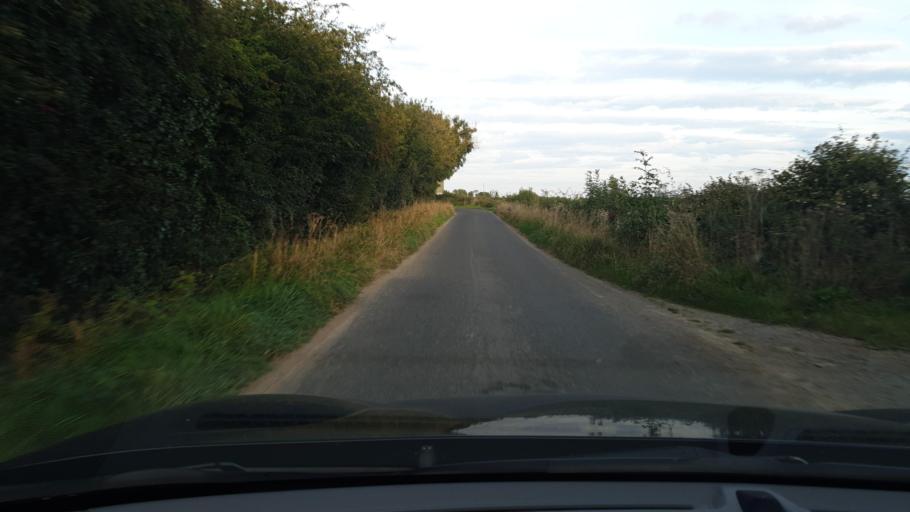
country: IE
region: Leinster
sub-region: An Mhi
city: Ashbourne
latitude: 53.5234
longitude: -6.3849
